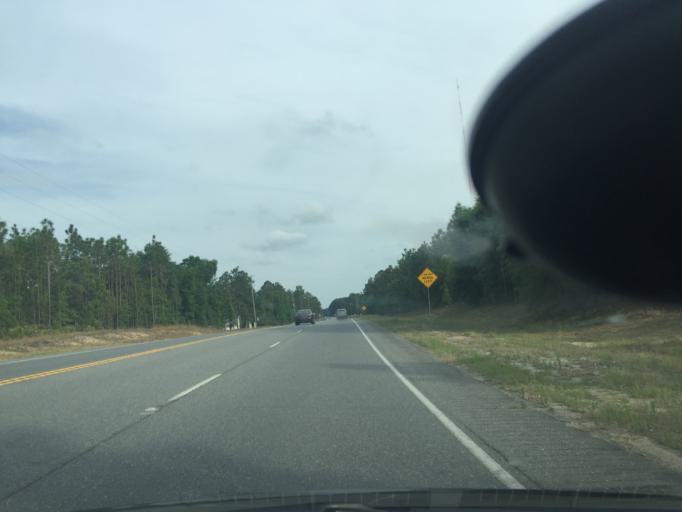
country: US
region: Georgia
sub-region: Chatham County
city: Bloomingdale
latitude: 32.0560
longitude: -81.3462
